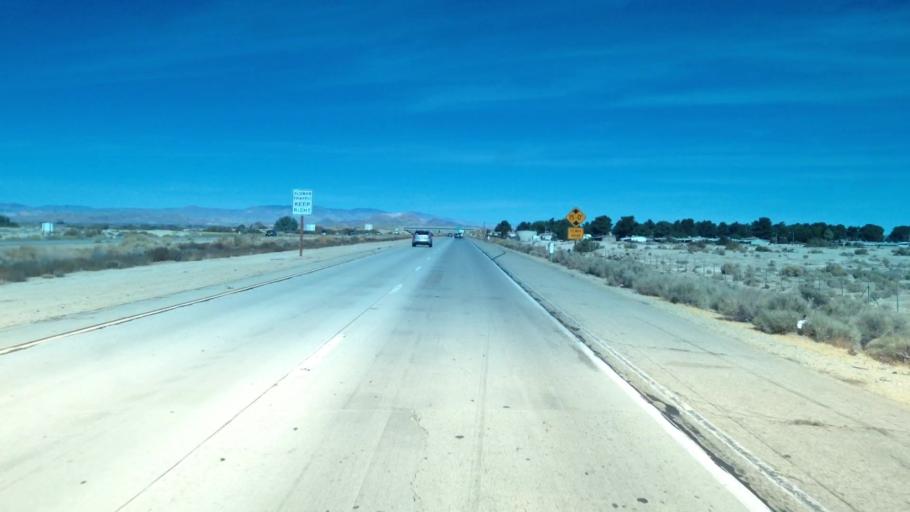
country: US
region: California
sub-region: Los Angeles County
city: Lancaster
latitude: 34.7539
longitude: -118.1703
